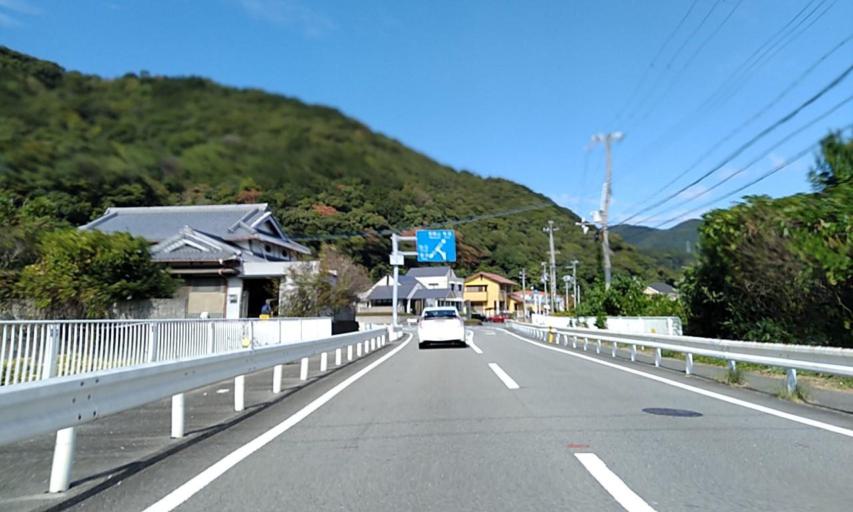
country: JP
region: Wakayama
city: Gobo
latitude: 33.9632
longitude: 135.1235
